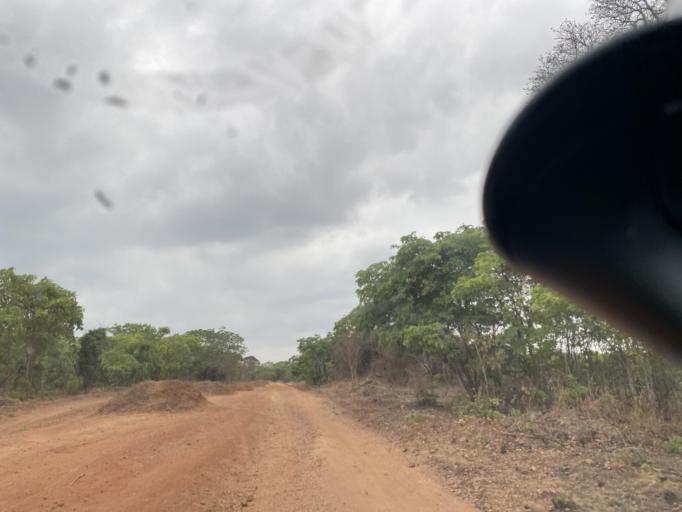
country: ZM
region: Lusaka
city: Chongwe
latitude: -15.2265
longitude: 28.7343
